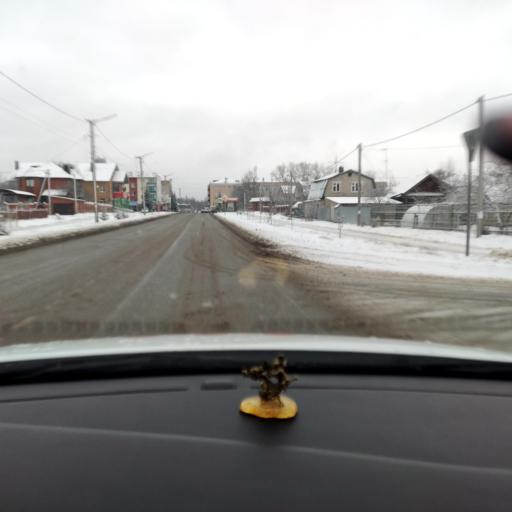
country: RU
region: Tatarstan
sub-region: Zelenodol'skiy Rayon
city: Zelenodolsk
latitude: 55.8539
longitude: 48.5306
